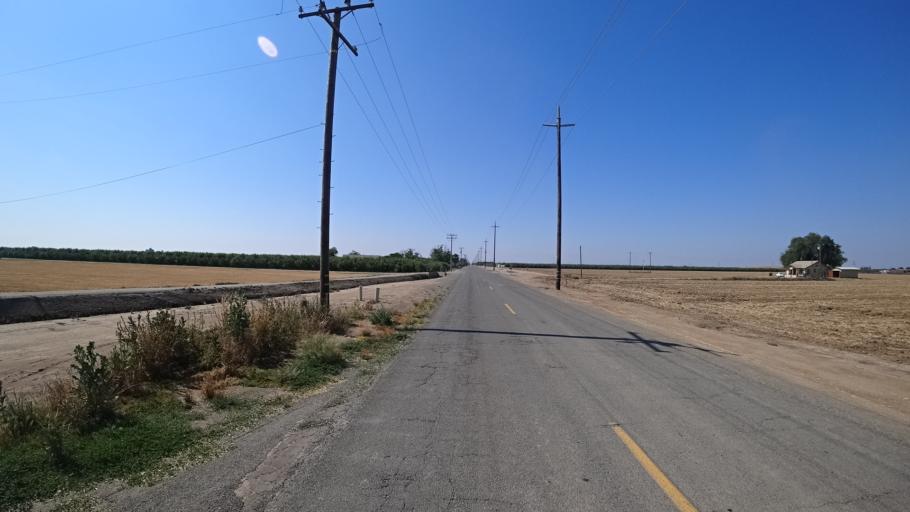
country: US
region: California
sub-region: Kings County
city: Hanford
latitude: 36.3643
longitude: -119.5831
